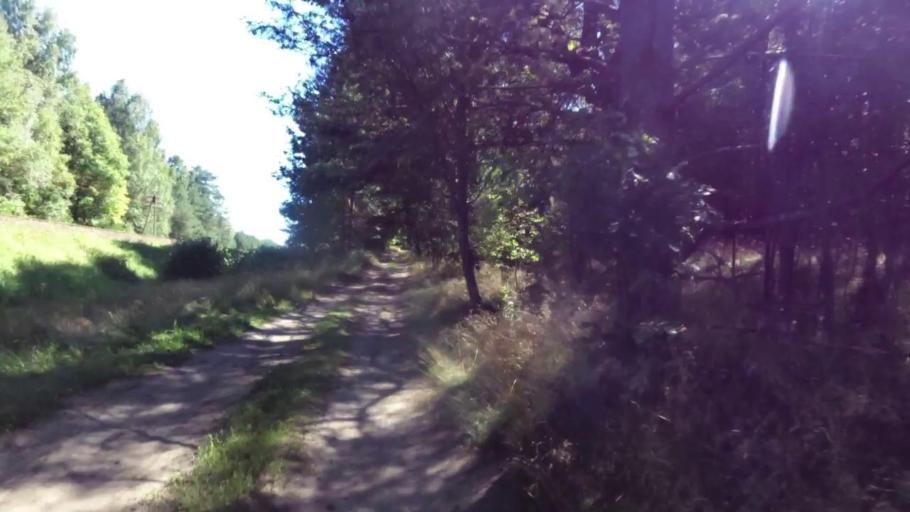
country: PL
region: West Pomeranian Voivodeship
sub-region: Powiat szczecinecki
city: Bialy Bor
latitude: 53.8394
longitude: 16.8732
